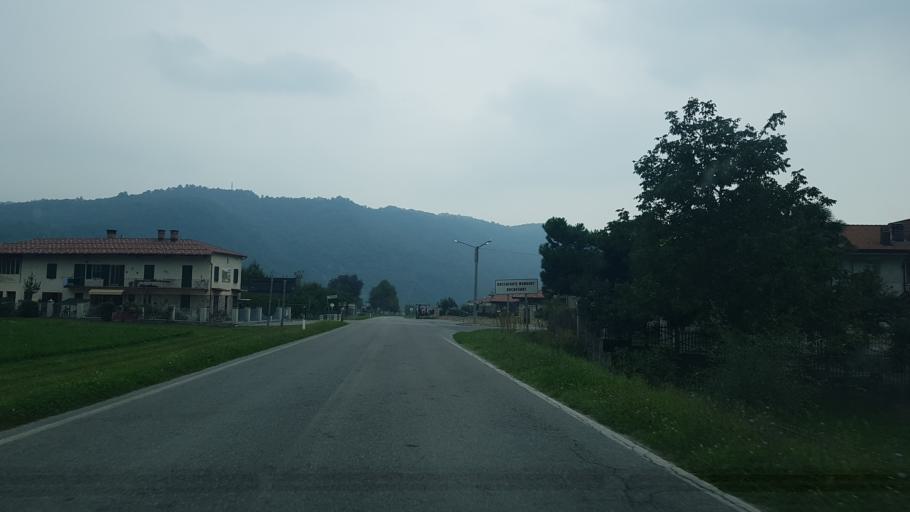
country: IT
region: Piedmont
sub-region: Provincia di Cuneo
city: Roccaforte Mondovi
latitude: 44.3114
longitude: 7.7444
